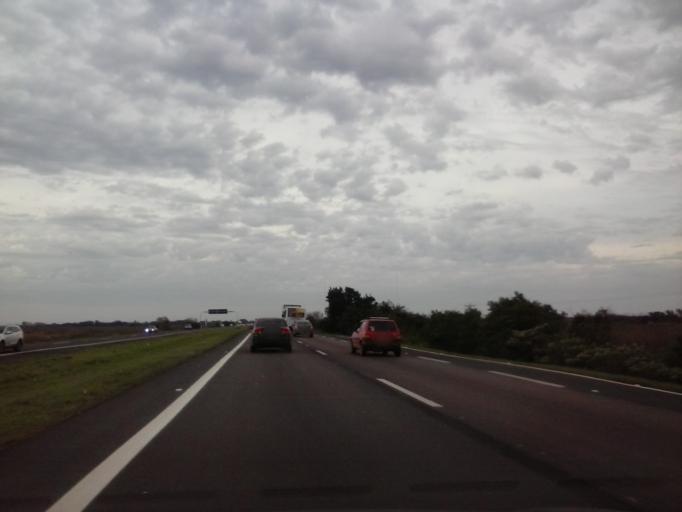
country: BR
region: Rio Grande do Sul
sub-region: Porto Alegre
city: Porto Alegre
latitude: -30.0010
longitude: -51.3017
